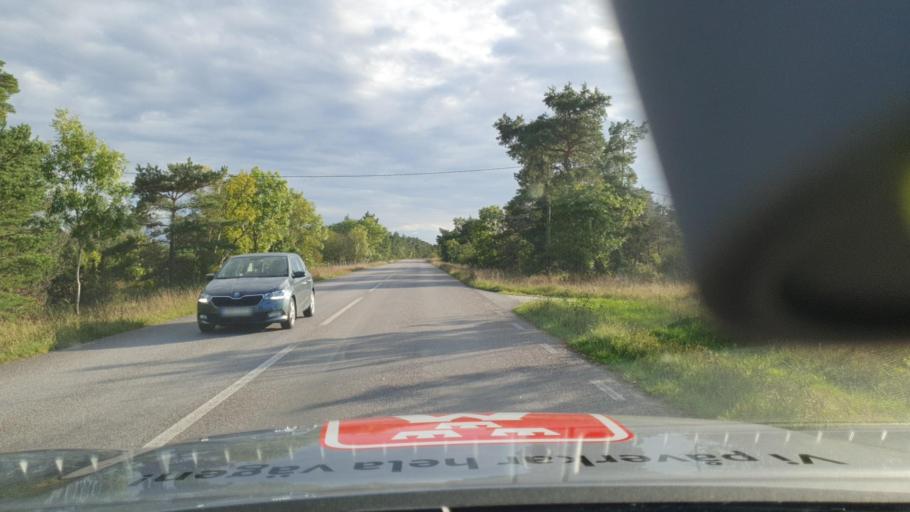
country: SE
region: Gotland
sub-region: Gotland
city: Slite
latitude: 57.4417
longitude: 18.6997
